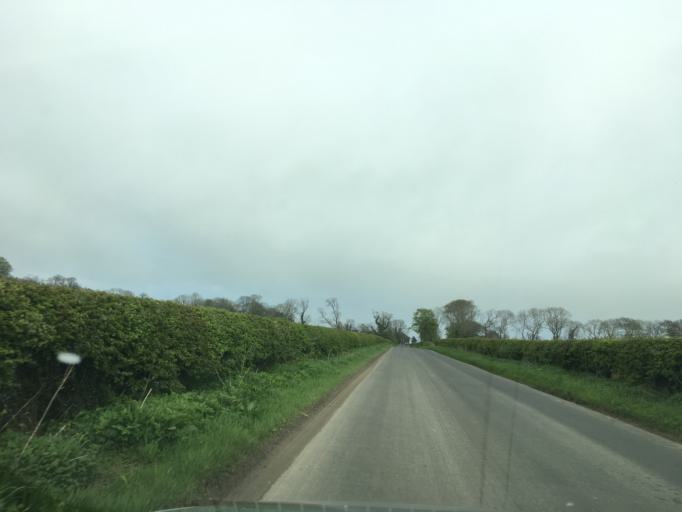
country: GB
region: Scotland
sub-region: Argyll and Bute
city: Port Bannatyne
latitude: 55.8584
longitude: -5.1216
